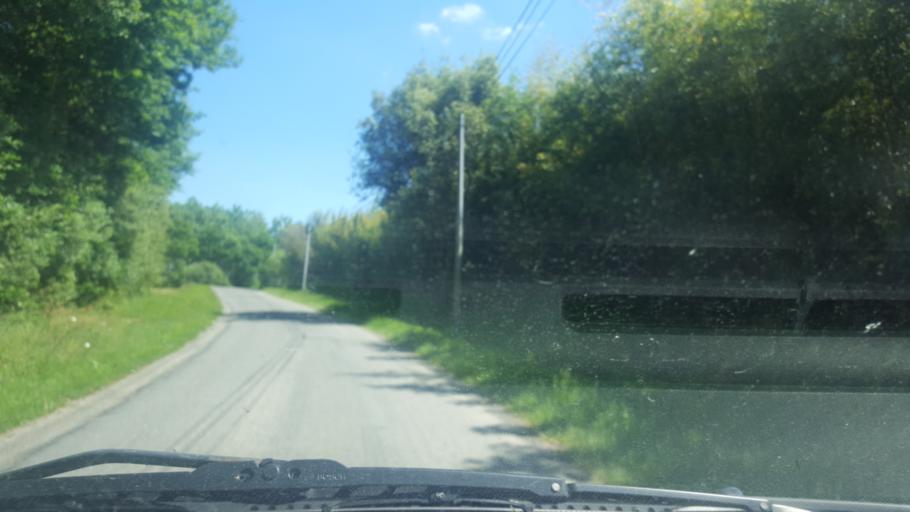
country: FR
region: Pays de la Loire
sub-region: Departement de la Loire-Atlantique
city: La Limouziniere
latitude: 47.0164
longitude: -1.6144
